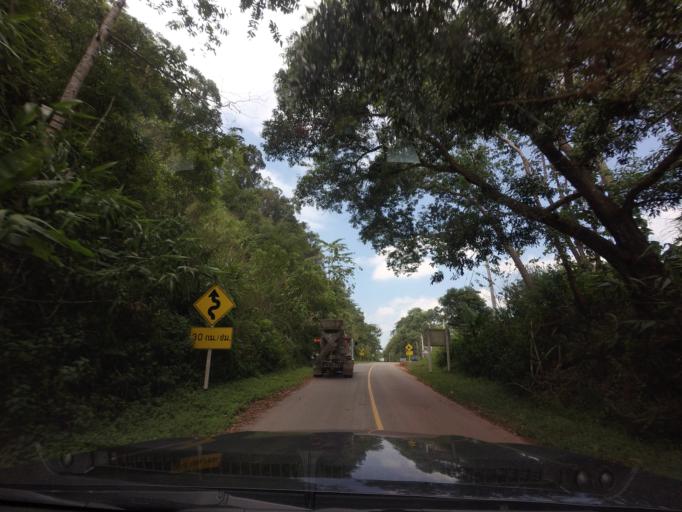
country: TH
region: Loei
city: Na Haeo
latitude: 17.4836
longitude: 100.9092
